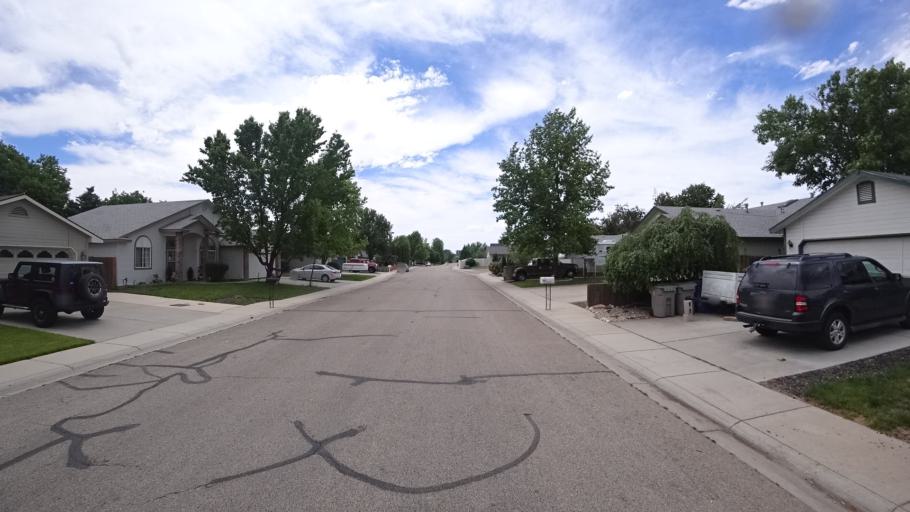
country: US
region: Idaho
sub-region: Ada County
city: Meridian
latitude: 43.6313
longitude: -116.3270
